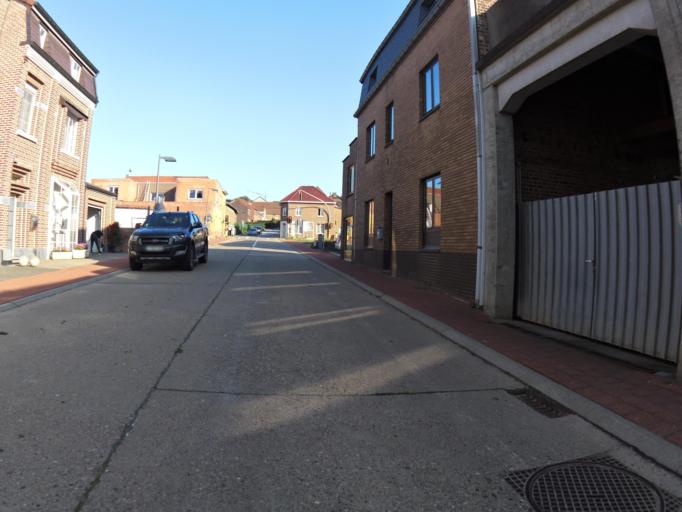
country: BE
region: Flanders
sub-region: Provincie Limburg
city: Riemst
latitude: 50.8037
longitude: 5.5745
